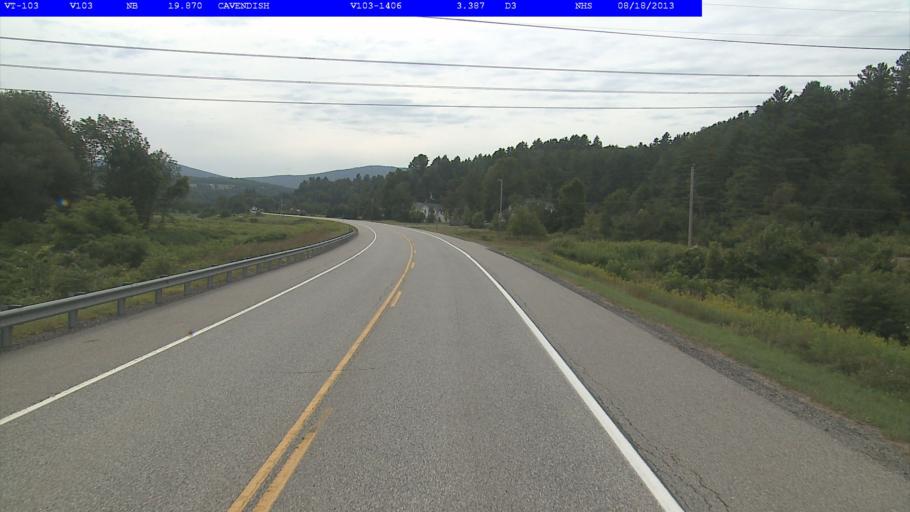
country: US
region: Vermont
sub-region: Windsor County
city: Chester
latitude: 43.3882
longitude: -72.6548
